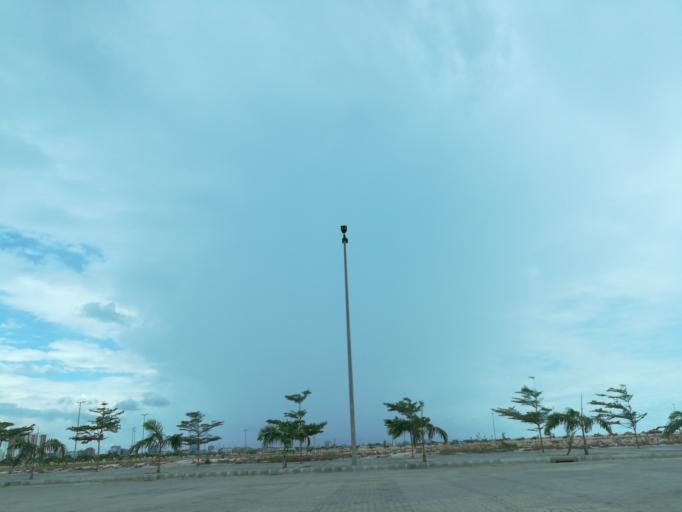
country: NG
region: Lagos
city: Ikoyi
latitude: 6.4088
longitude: 3.4180
